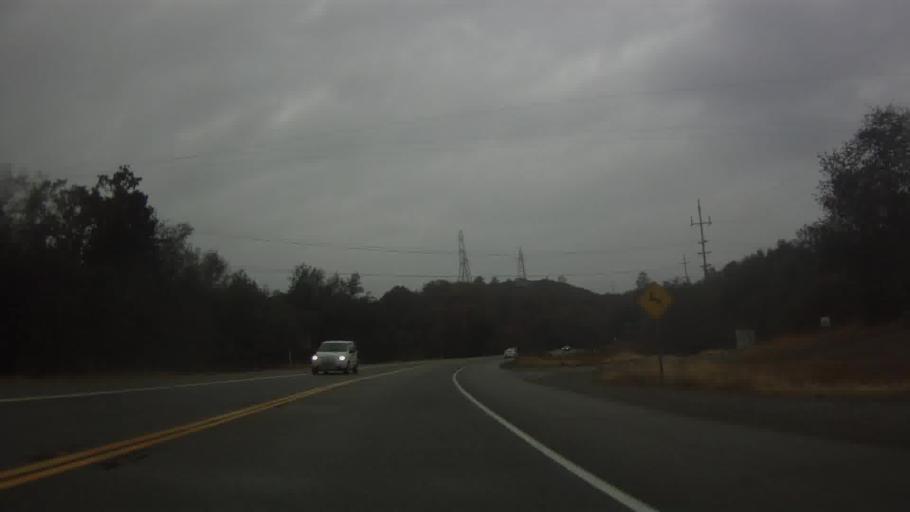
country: US
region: California
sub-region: Shasta County
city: Redding
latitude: 40.5820
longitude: -122.4341
